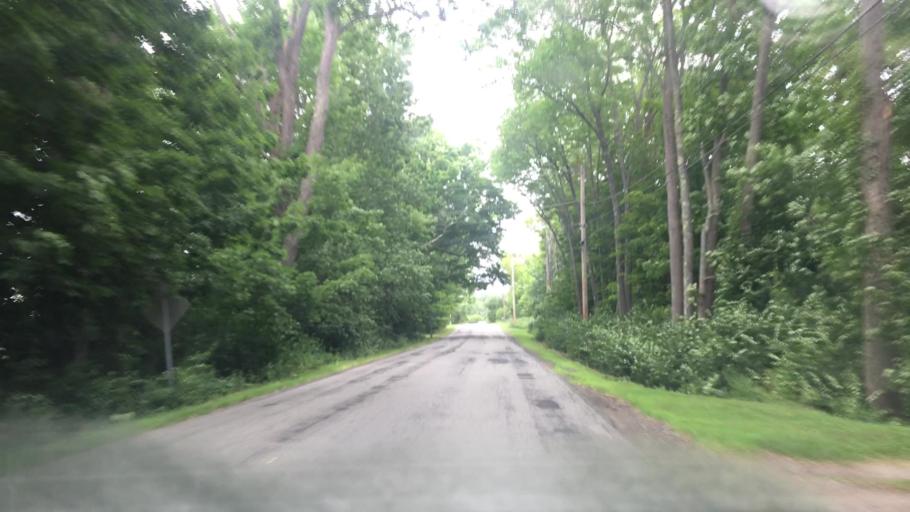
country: US
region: Maine
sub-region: Penobscot County
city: Veazie
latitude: 44.8476
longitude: -68.7468
